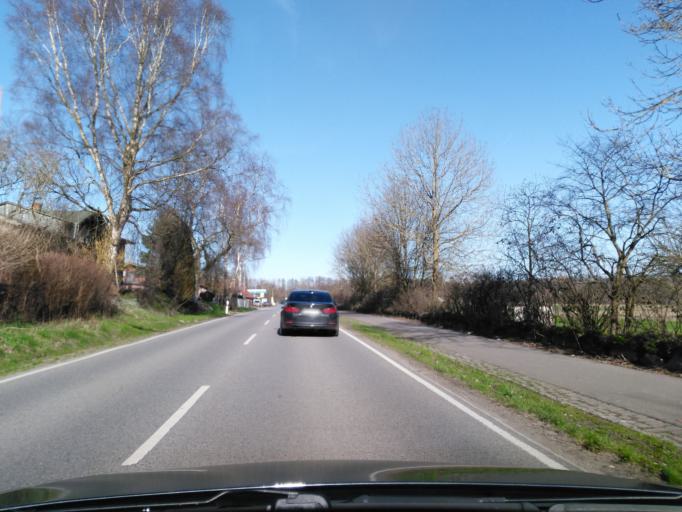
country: DE
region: Schleswig-Holstein
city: Achterwehr
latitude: 54.3158
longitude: 9.9553
